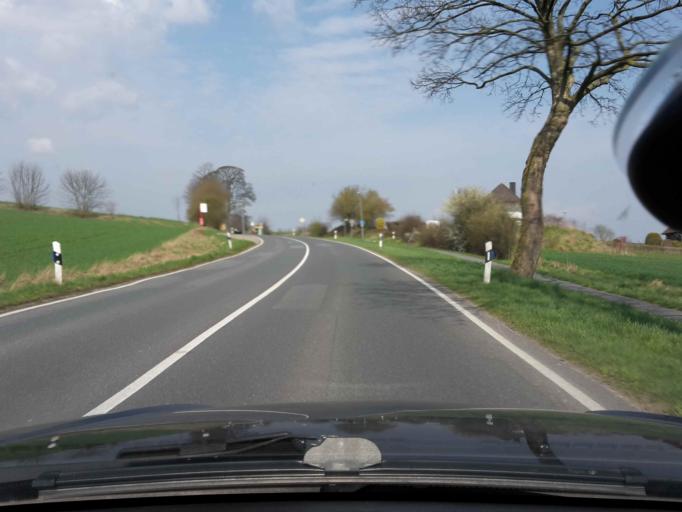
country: DE
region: Lower Saxony
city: Harmstorf
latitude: 53.3735
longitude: 9.9841
